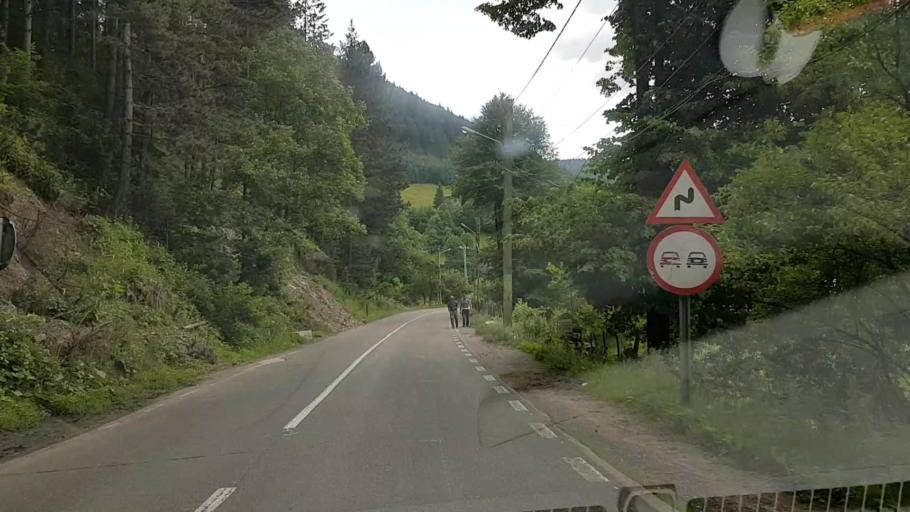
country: RO
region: Suceava
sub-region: Comuna Brosteni
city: Brosteni
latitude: 47.2302
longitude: 25.7443
